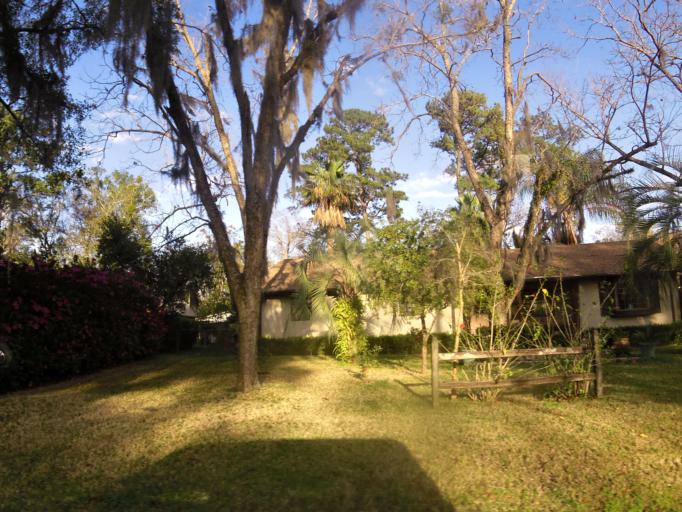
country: US
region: Florida
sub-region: Duval County
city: Jacksonville
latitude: 30.2607
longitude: -81.5833
